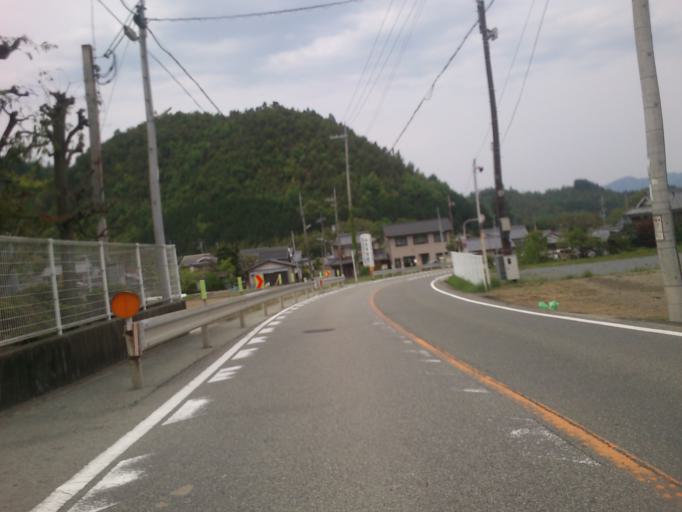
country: JP
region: Kyoto
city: Kameoka
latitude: 34.9935
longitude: 135.5363
